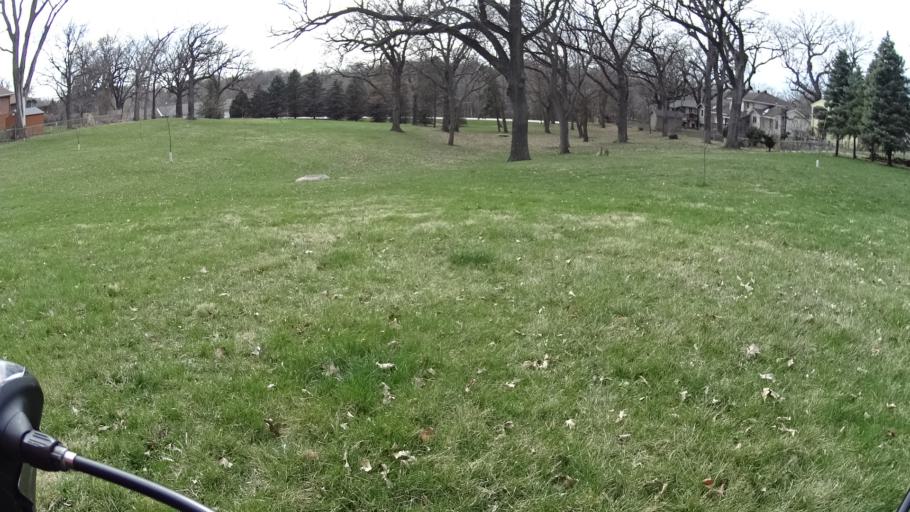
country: US
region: Nebraska
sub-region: Sarpy County
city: Offutt Air Force Base
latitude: 41.1171
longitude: -95.9648
